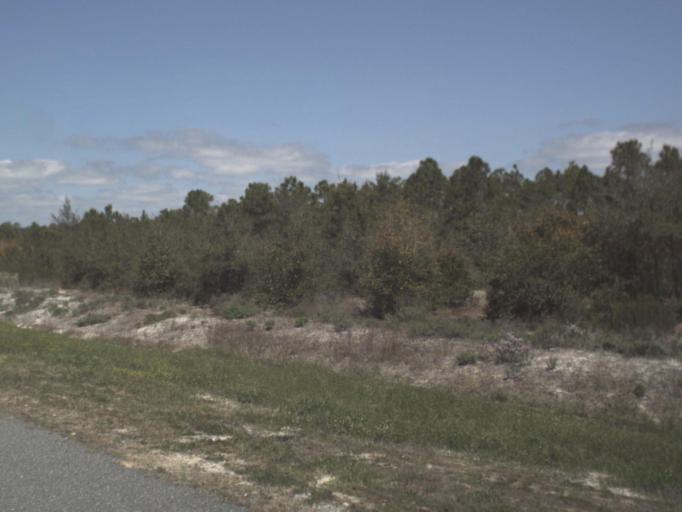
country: US
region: Florida
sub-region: Gulf County
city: Port Saint Joe
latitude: 29.8654
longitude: -85.3378
